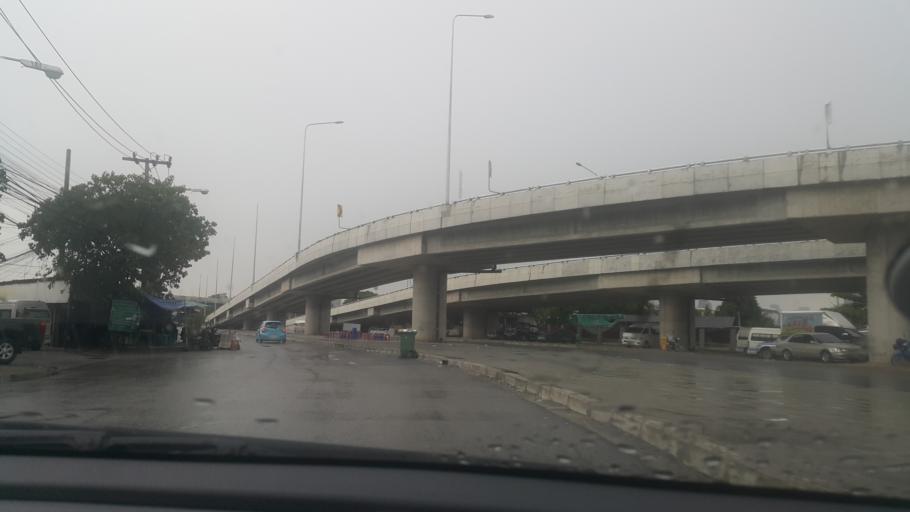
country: TH
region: Bangkok
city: Bang Sue
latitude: 13.8115
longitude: 100.5459
